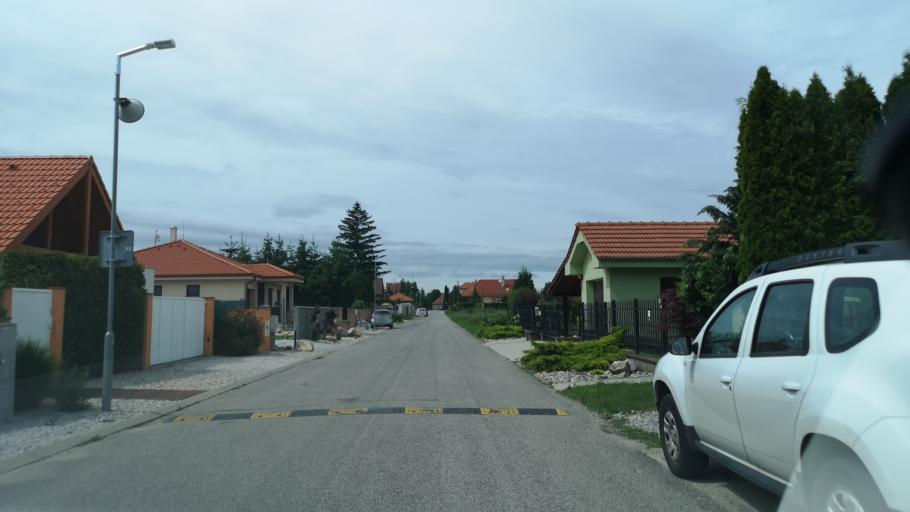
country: SK
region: Nitriansky
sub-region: Okres Nitra
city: Nitra
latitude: 48.3538
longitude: 18.0262
